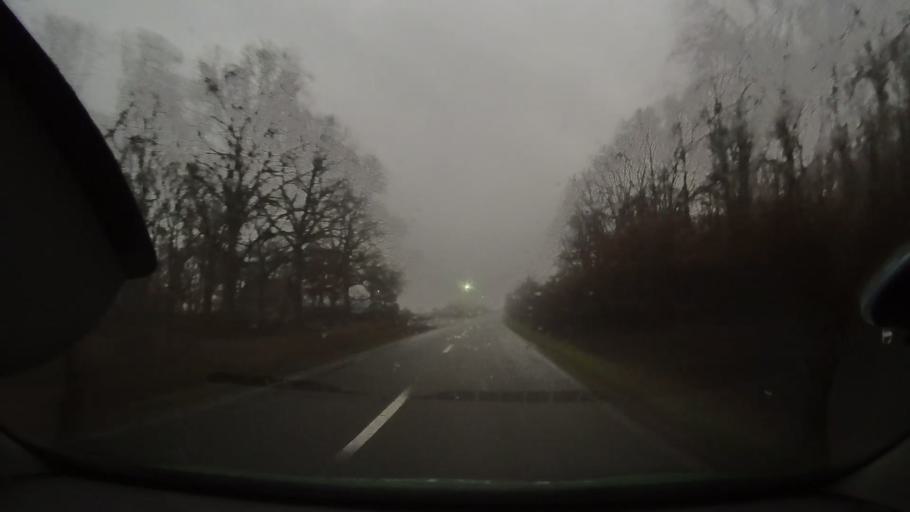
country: RO
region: Arad
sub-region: Comuna Beliu
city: Beliu
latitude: 46.5017
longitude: 21.9734
